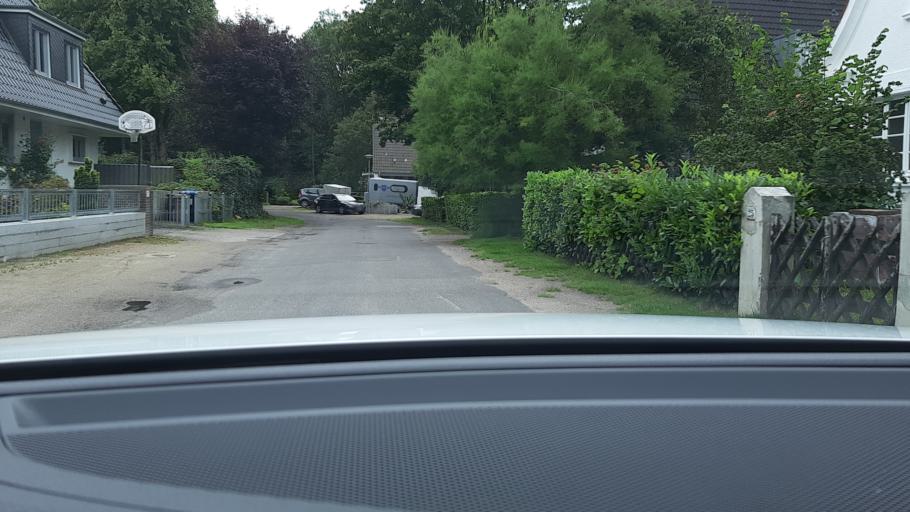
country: DE
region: Schleswig-Holstein
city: Bad Schwartau
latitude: 53.9006
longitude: 10.7373
